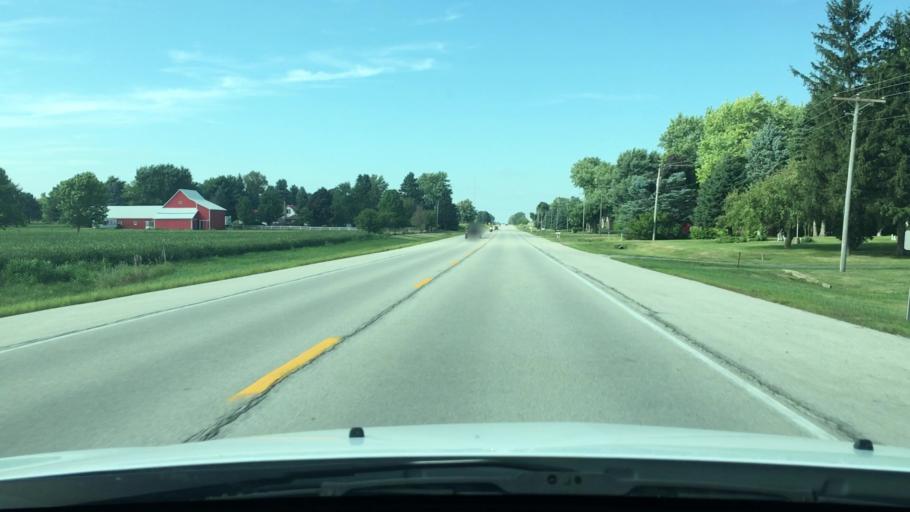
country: US
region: Illinois
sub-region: DeKalb County
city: DeKalb
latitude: 41.8516
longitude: -88.7539
